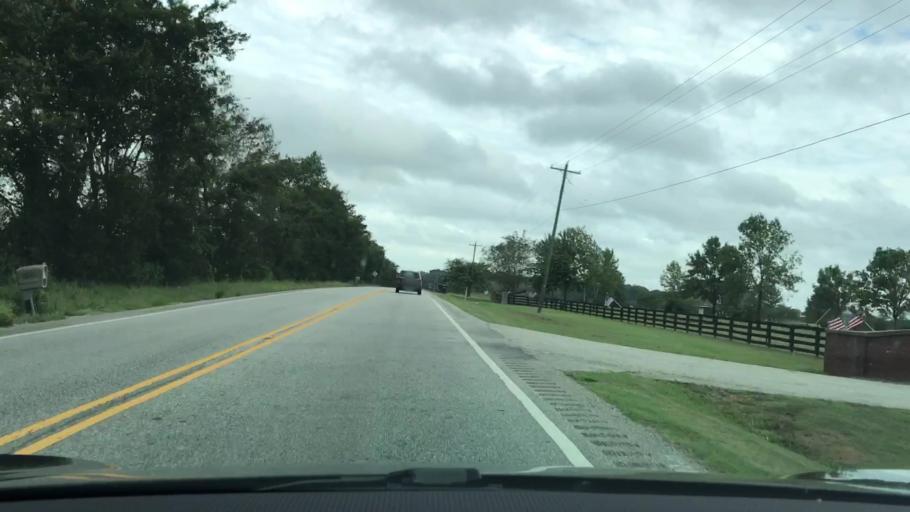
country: US
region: Alabama
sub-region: Montgomery County
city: Pike Road
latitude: 32.3184
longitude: -86.0476
